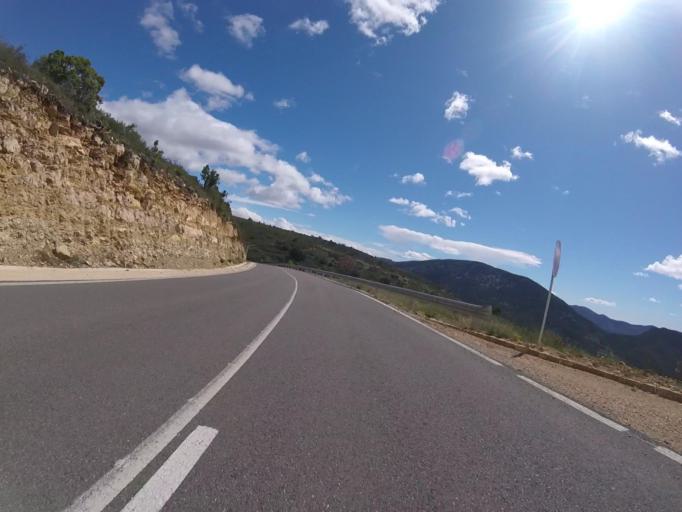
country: ES
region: Valencia
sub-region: Provincia de Castello
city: Culla
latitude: 40.3000
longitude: -0.1254
